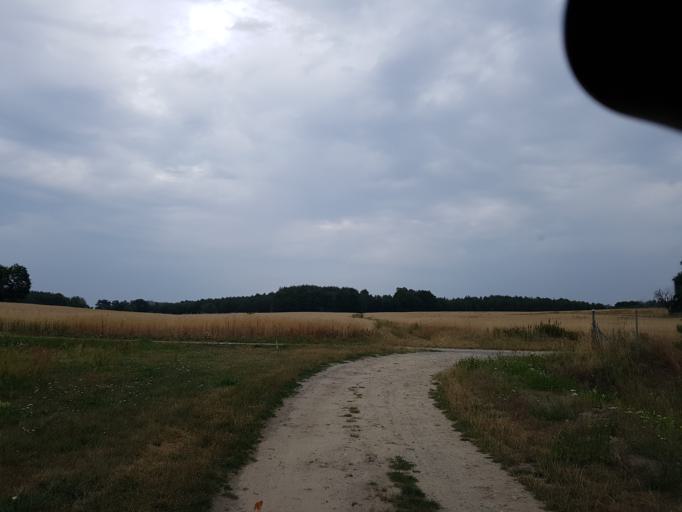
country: DE
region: Brandenburg
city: Sallgast
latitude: 51.5990
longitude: 13.7817
